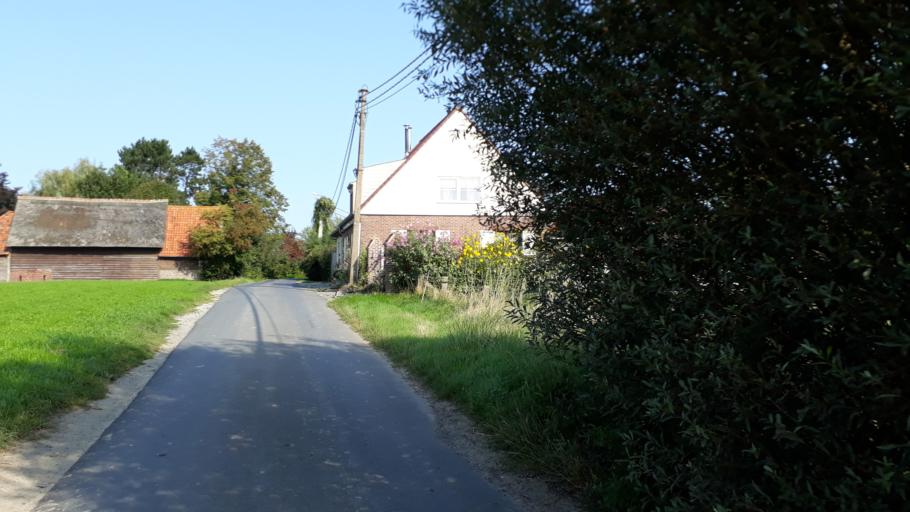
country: BE
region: Flanders
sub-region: Provincie West-Vlaanderen
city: Kortemark
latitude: 51.0253
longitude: 3.0769
